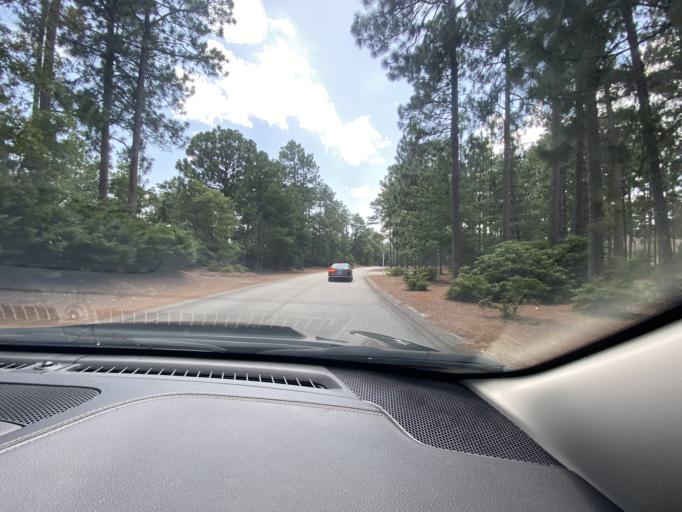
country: US
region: North Carolina
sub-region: Moore County
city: Pinehurst
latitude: 35.1871
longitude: -79.4348
